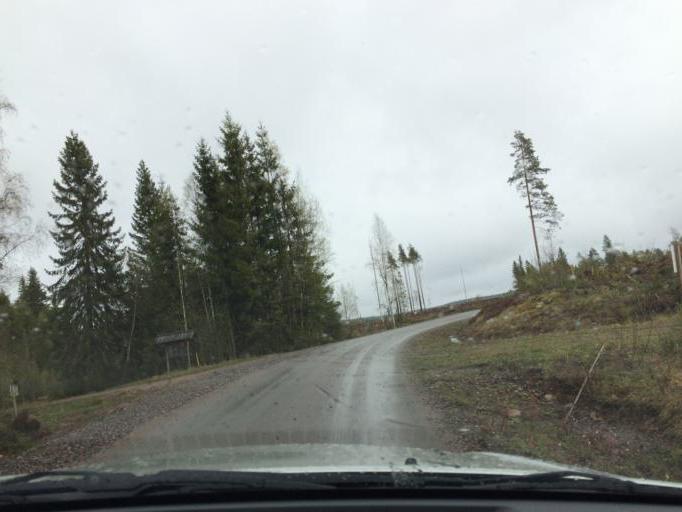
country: SE
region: Dalarna
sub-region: Ludvika Kommun
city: Abborrberget
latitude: 60.0186
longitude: 14.5987
